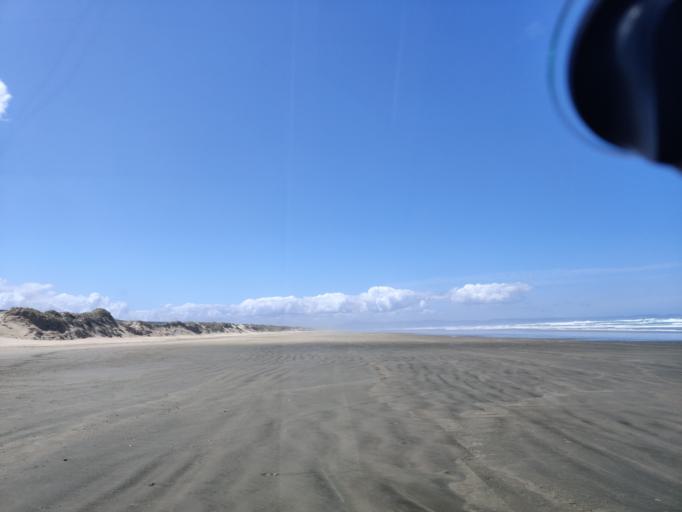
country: NZ
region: Northland
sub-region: Far North District
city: Kaitaia
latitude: -34.9536
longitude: 173.1236
